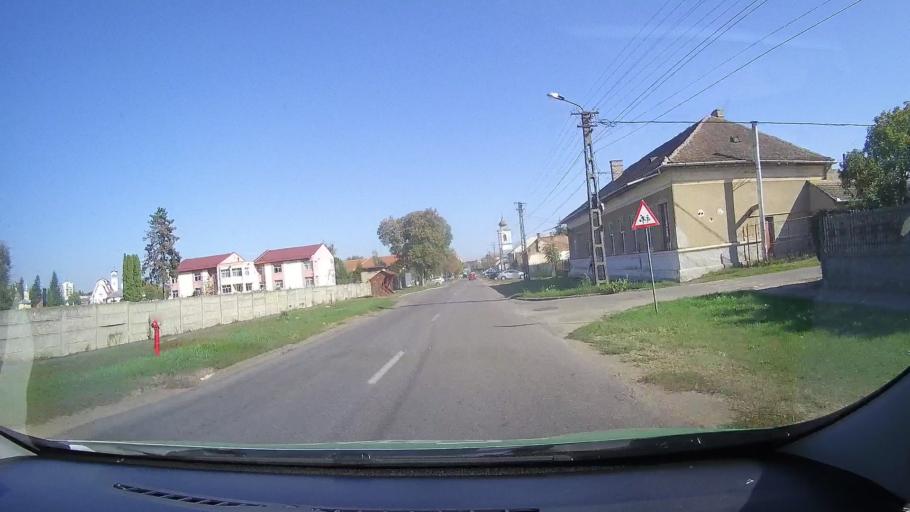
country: RO
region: Satu Mare
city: Carei
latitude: 47.6766
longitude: 22.4698
